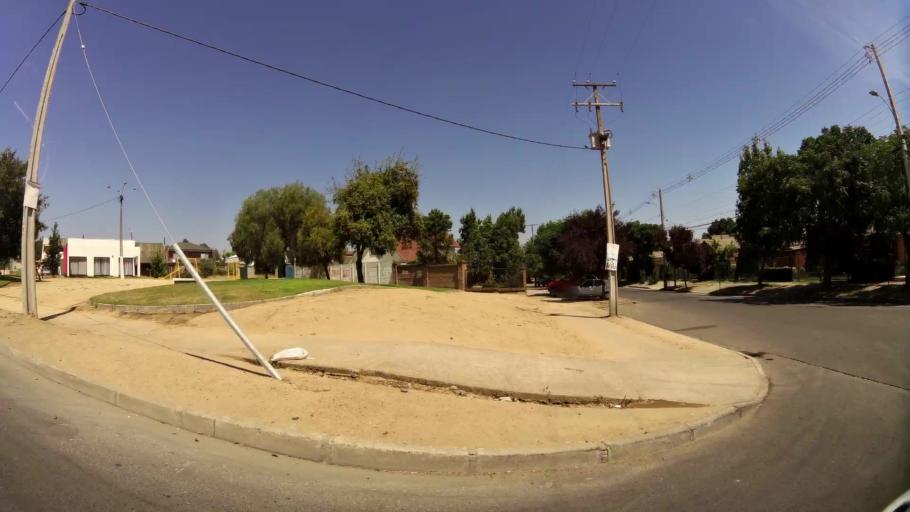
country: CL
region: Maule
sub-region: Provincia de Talca
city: Talca
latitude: -35.4244
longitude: -71.6253
